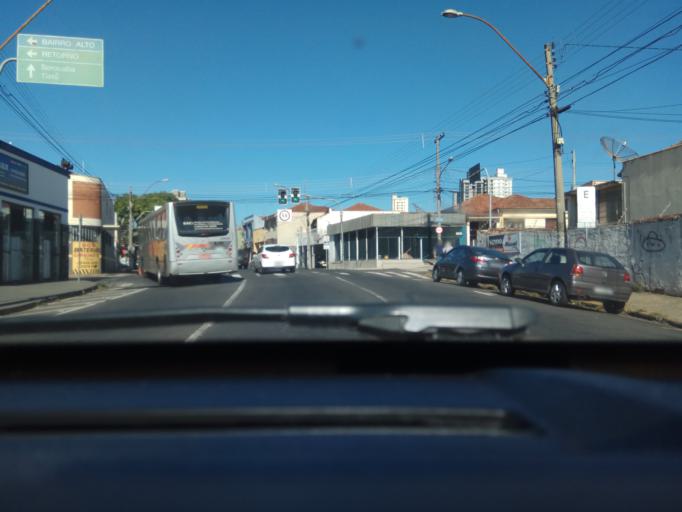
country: BR
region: Sao Paulo
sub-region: Piracicaba
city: Piracicaba
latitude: -22.7315
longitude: -47.6489
